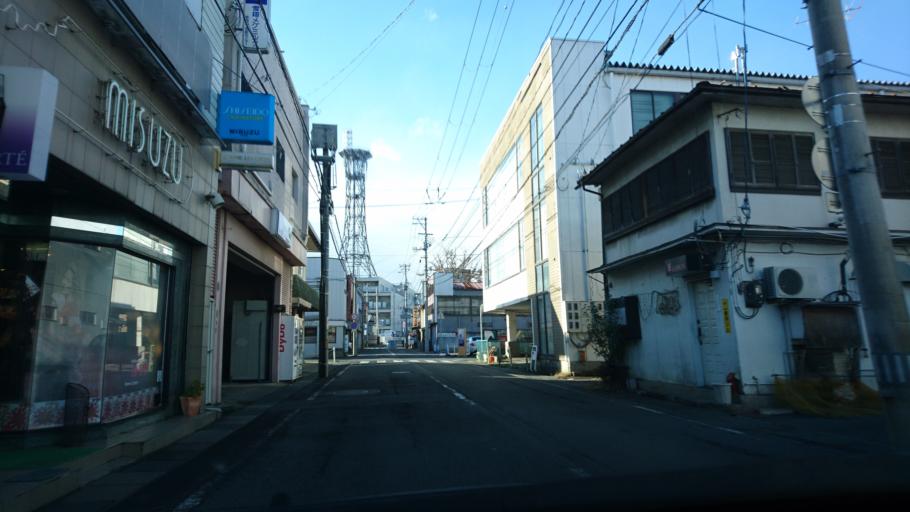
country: JP
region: Iwate
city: Mizusawa
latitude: 39.1419
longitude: 141.1445
